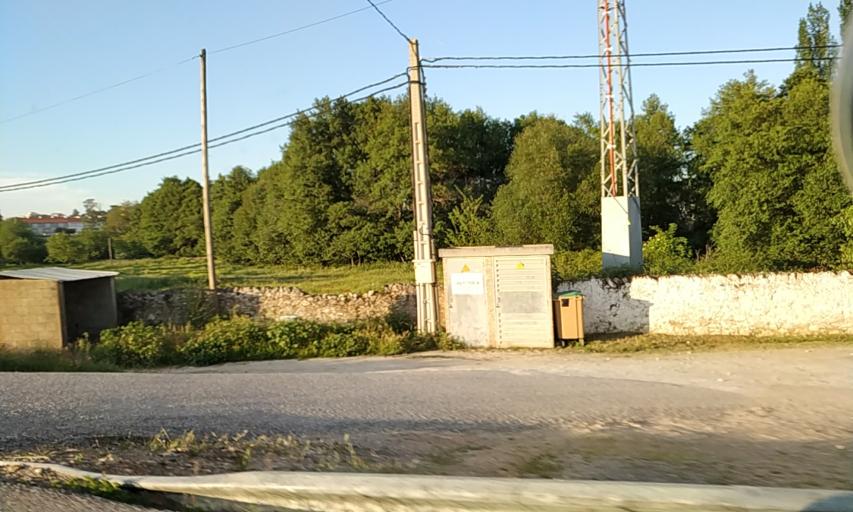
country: ES
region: Extremadura
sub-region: Provincia de Caceres
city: Valencia de Alcantara
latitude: 39.3982
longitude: -7.2499
